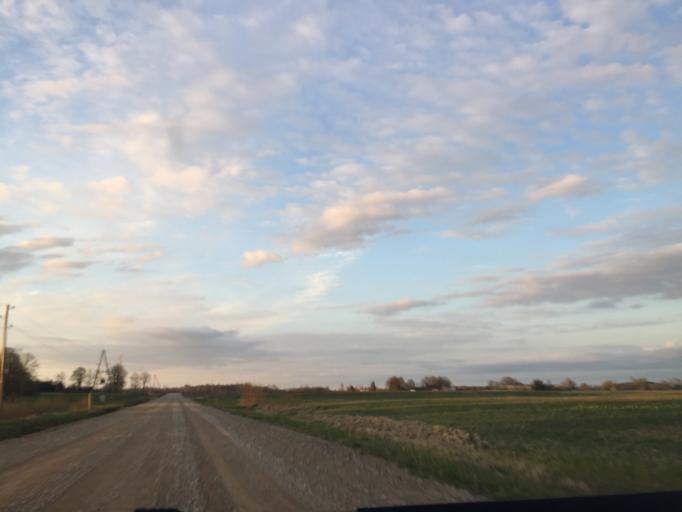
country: LV
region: Gulbenes Rajons
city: Gulbene
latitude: 57.1957
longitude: 26.7618
